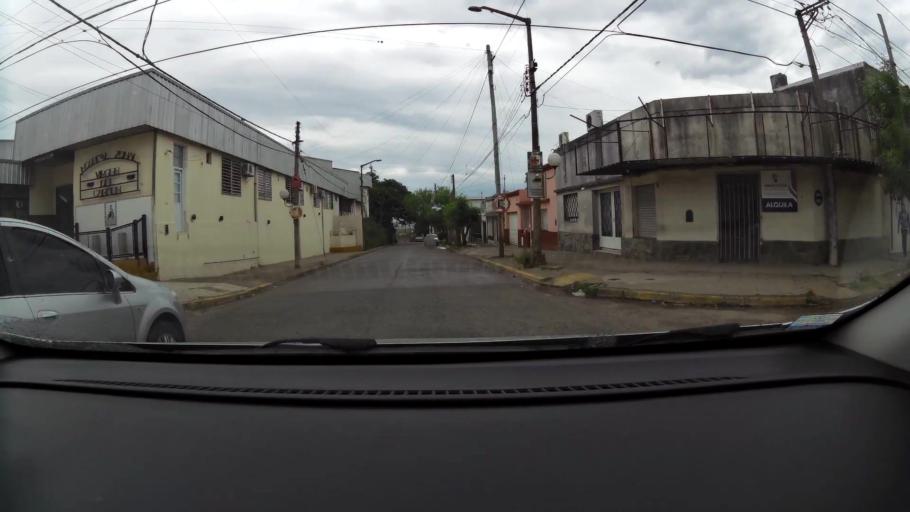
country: AR
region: Buenos Aires
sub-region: Partido de Zarate
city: Zarate
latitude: -34.0837
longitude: -59.0341
